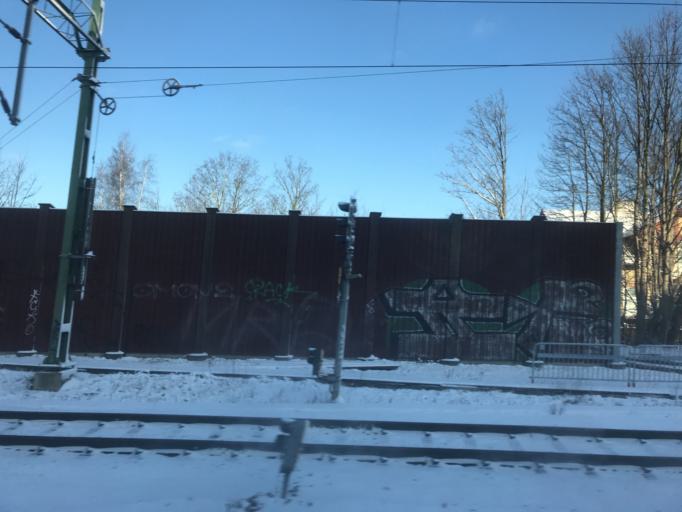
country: SE
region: Skane
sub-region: Burlovs Kommun
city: Arloev
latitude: 55.6316
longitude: 13.0642
